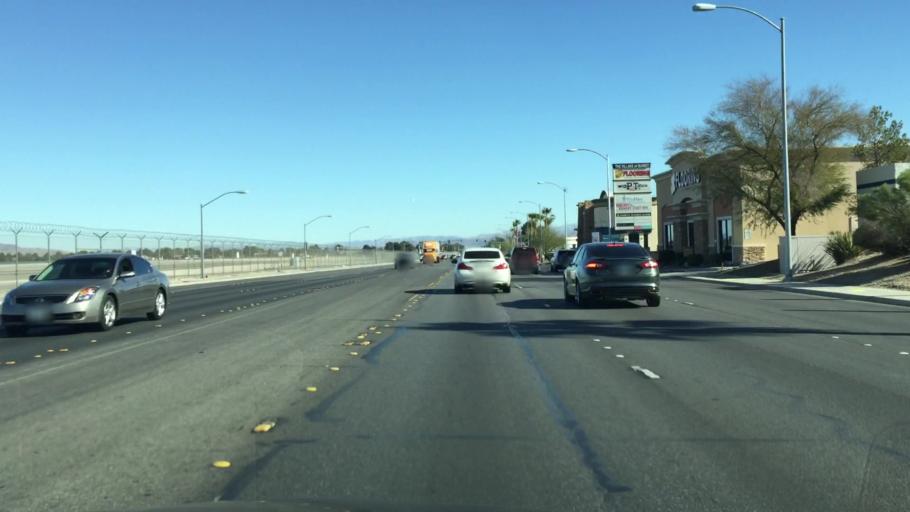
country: US
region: Nevada
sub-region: Clark County
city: Paradise
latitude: 36.0717
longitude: -115.1315
